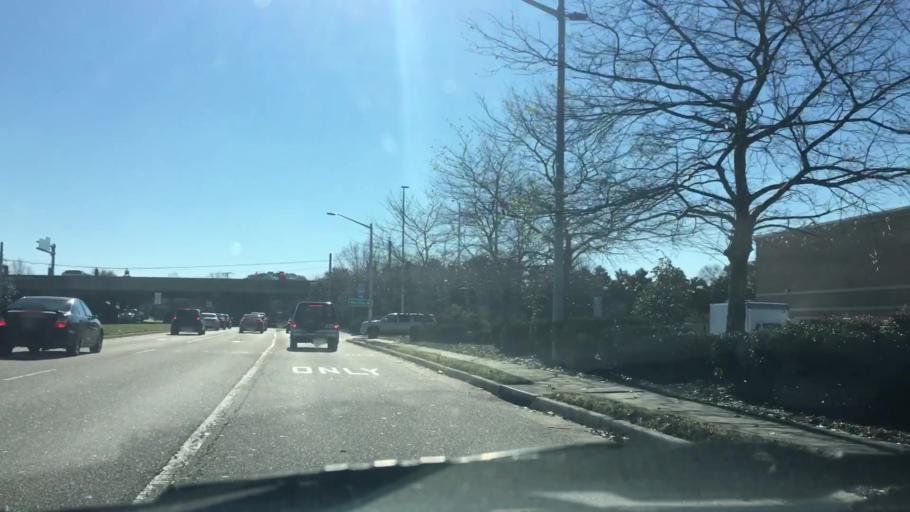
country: US
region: Virginia
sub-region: City of Virginia Beach
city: Virginia Beach
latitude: 36.8469
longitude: -76.0212
